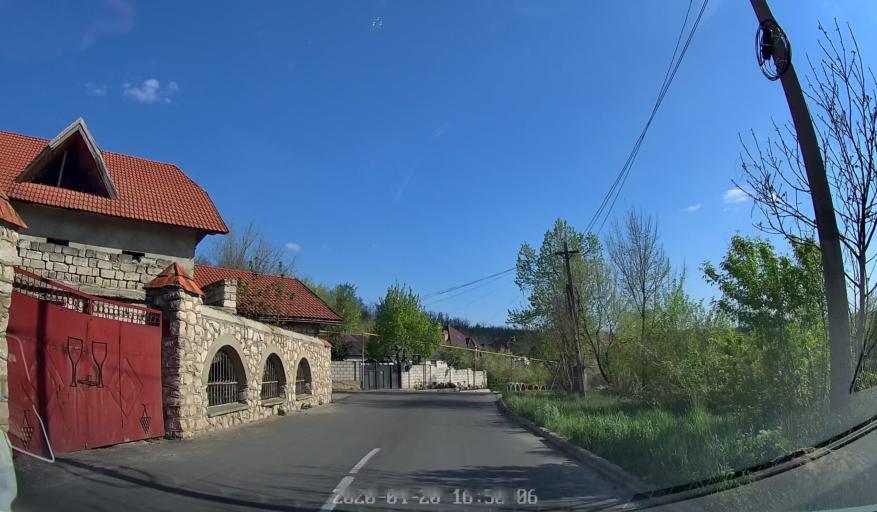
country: MD
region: Chisinau
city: Chisinau
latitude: 46.9683
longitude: 28.8507
